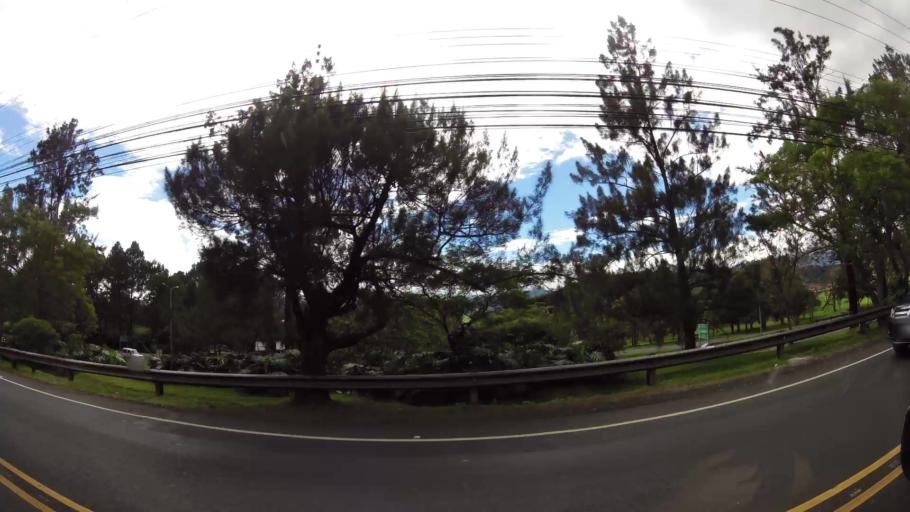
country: CR
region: San Jose
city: Curridabat
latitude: 9.9131
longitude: -84.0270
